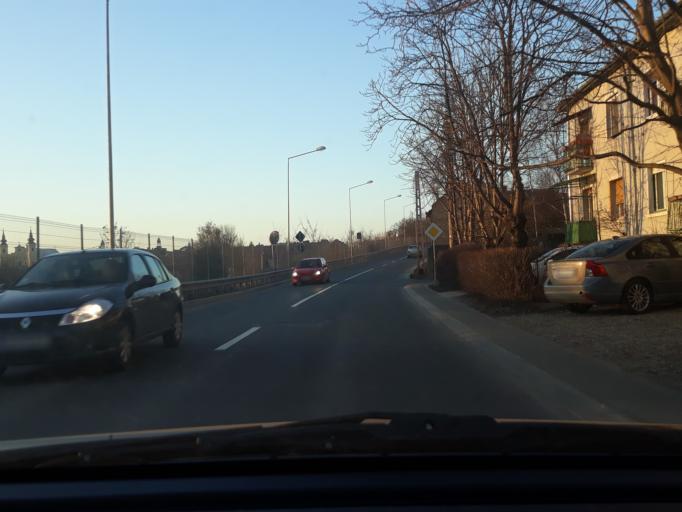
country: RO
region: Bihor
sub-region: Comuna Biharea
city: Oradea
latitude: 47.0639
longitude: 21.9397
